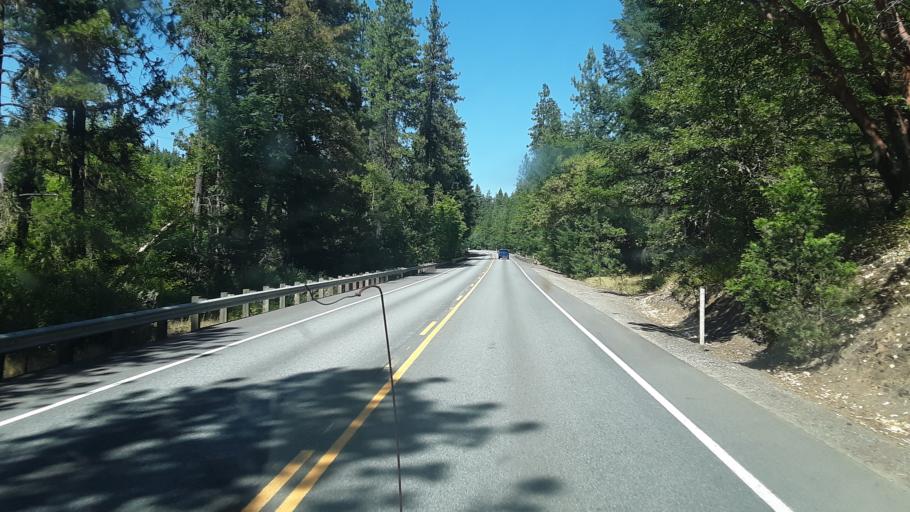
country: US
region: Oregon
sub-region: Josephine County
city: Cave Junction
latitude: 42.3181
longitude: -123.6016
